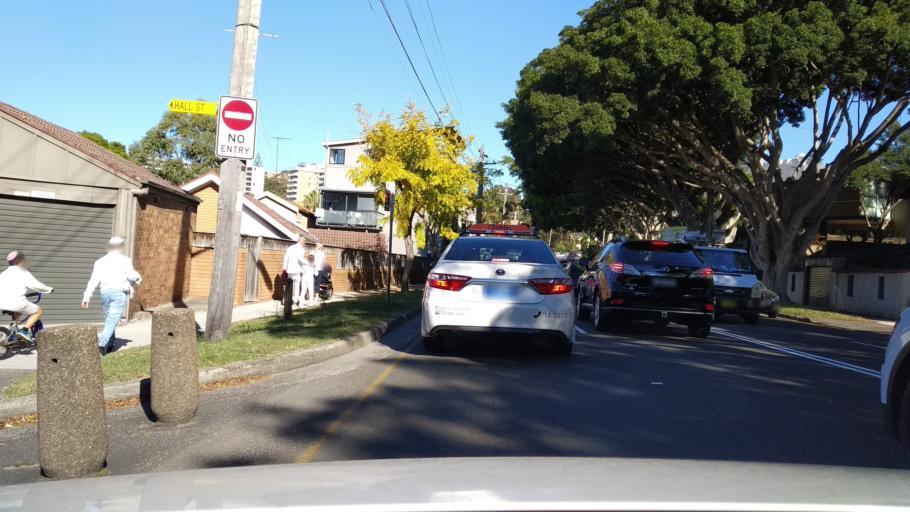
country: AU
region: New South Wales
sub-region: Waverley
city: Bondi Beach
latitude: -33.8871
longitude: 151.2658
